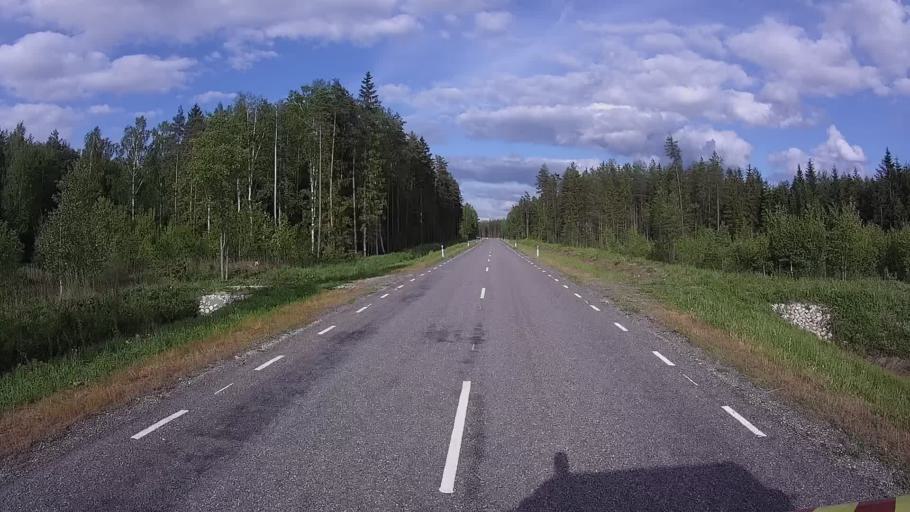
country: EE
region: Jogevamaa
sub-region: Mustvee linn
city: Mustvee
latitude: 59.0224
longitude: 27.0609
